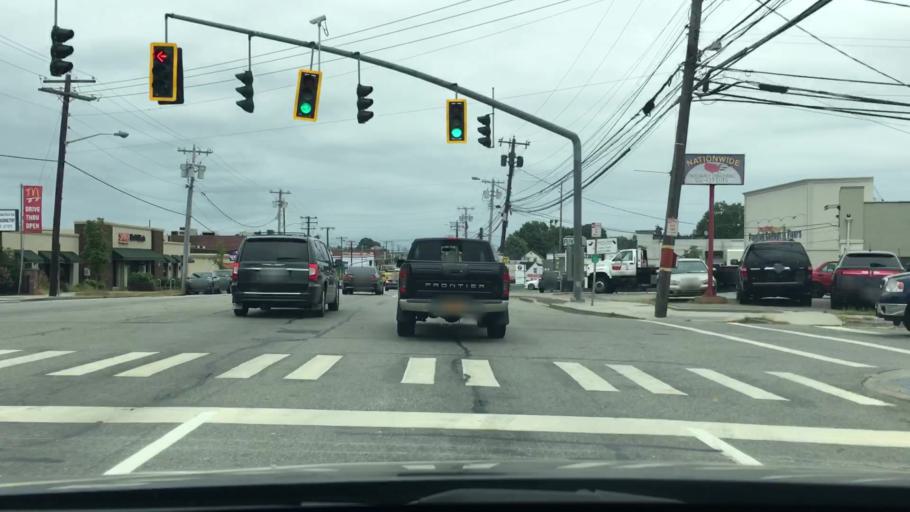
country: US
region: New York
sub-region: Nassau County
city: Garden City Park
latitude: 40.7360
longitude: -73.6733
